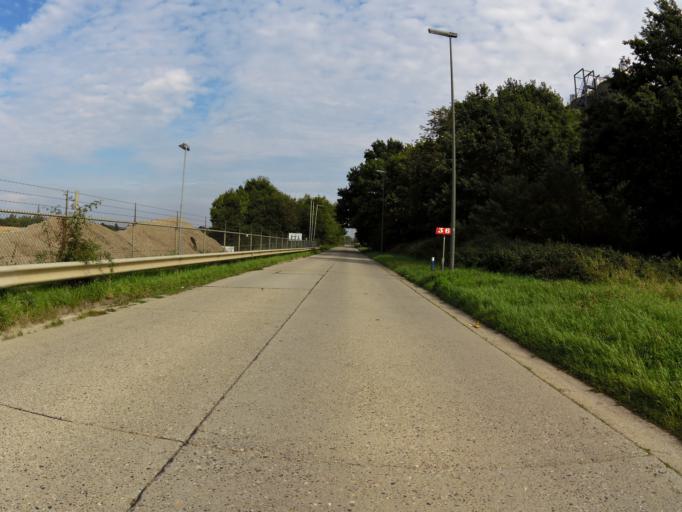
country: BE
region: Flanders
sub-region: Provincie Limburg
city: Lanaken
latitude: 50.8811
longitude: 5.6495
